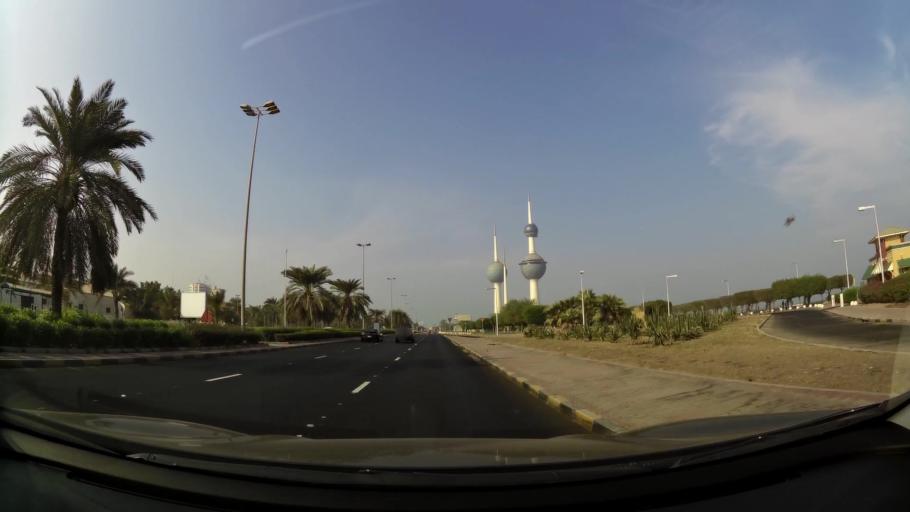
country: KW
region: Al Asimah
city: Ad Dasmah
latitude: 29.3849
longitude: 48.0026
